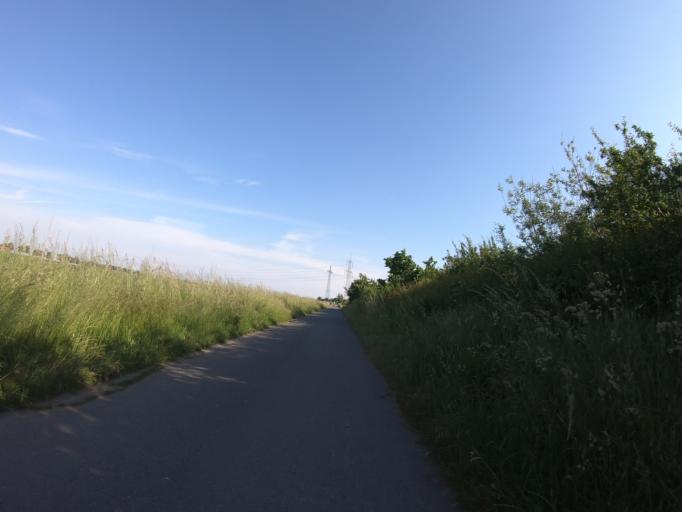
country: DE
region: Lower Saxony
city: Meine
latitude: 52.3742
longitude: 10.5434
